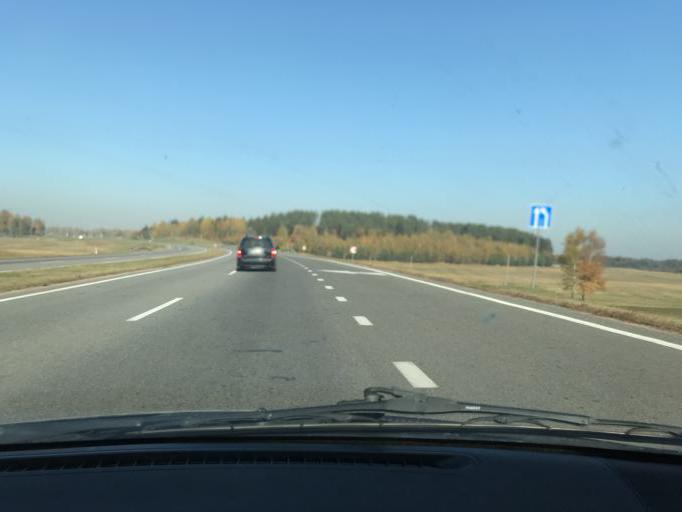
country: BY
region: Minsk
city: Samakhvalavichy
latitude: 53.6975
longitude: 27.5258
